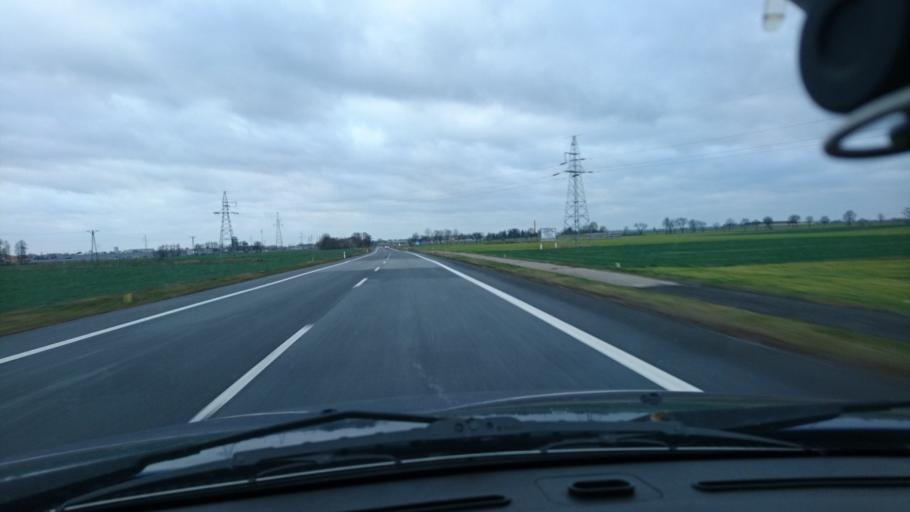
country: PL
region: Opole Voivodeship
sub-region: Powiat kluczborski
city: Kluczbork
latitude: 50.9902
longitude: 18.2255
